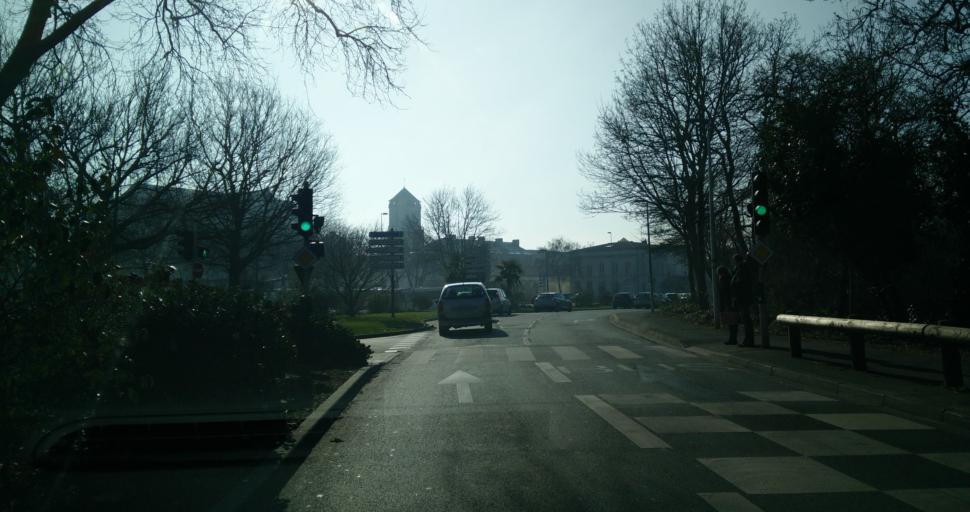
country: FR
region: Poitou-Charentes
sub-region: Departement de la Charente-Maritime
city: La Rochelle
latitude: 46.1633
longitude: -1.1553
